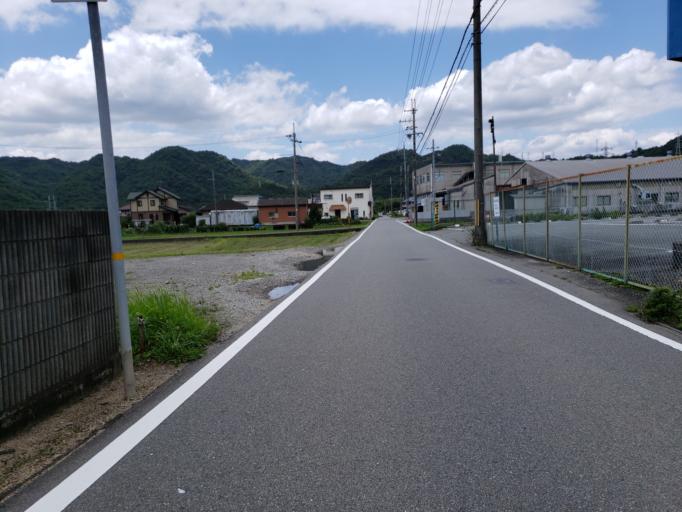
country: JP
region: Hyogo
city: Himeji
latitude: 34.8857
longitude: 134.7346
